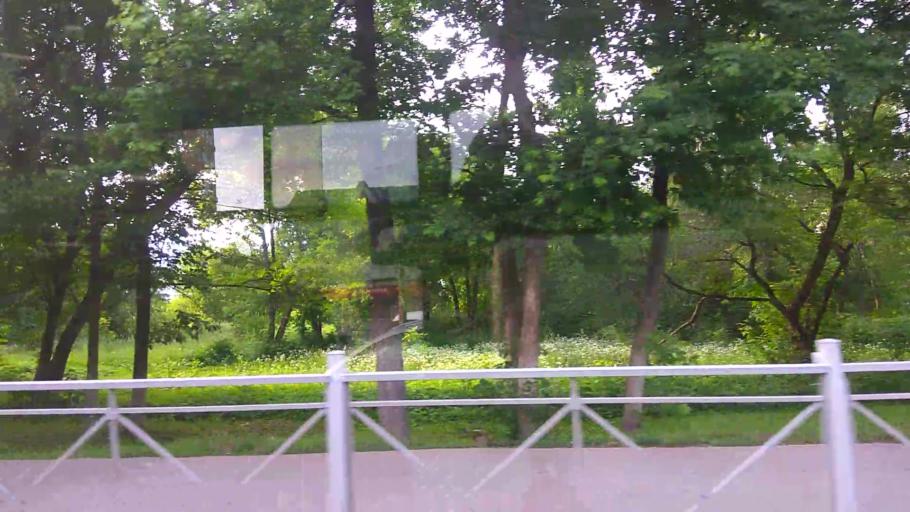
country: RU
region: Moskovskaya
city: Mytishchi
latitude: 55.9161
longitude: 37.7529
